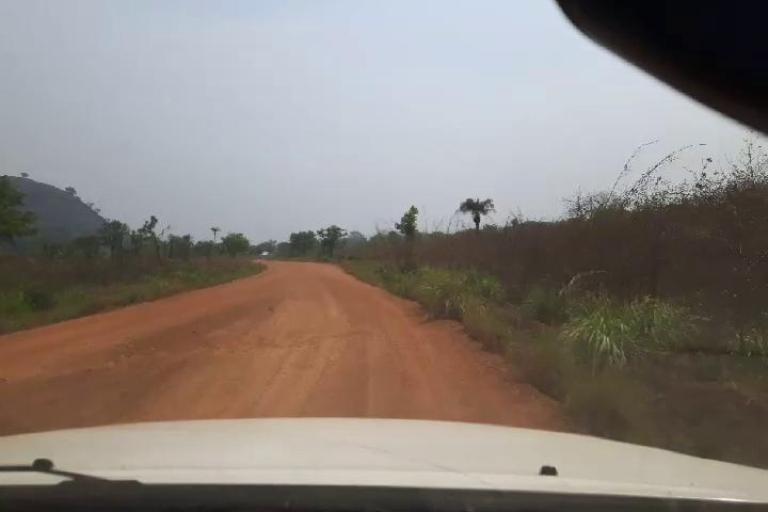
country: SL
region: Northern Province
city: Bumbuna
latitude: 8.9541
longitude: -11.8055
